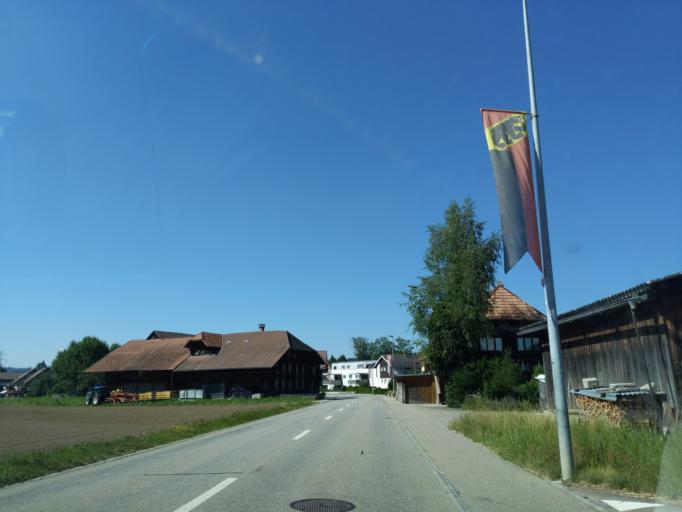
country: CH
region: Bern
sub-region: Emmental District
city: Lauperswil
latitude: 46.9719
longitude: 7.7403
